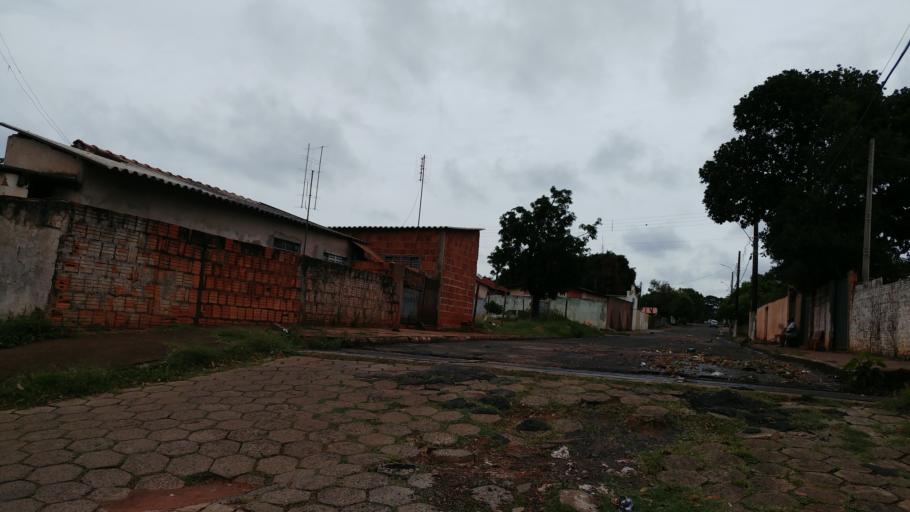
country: BR
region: Sao Paulo
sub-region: Paraguacu Paulista
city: Paraguacu Paulista
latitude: -22.4106
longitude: -50.5650
